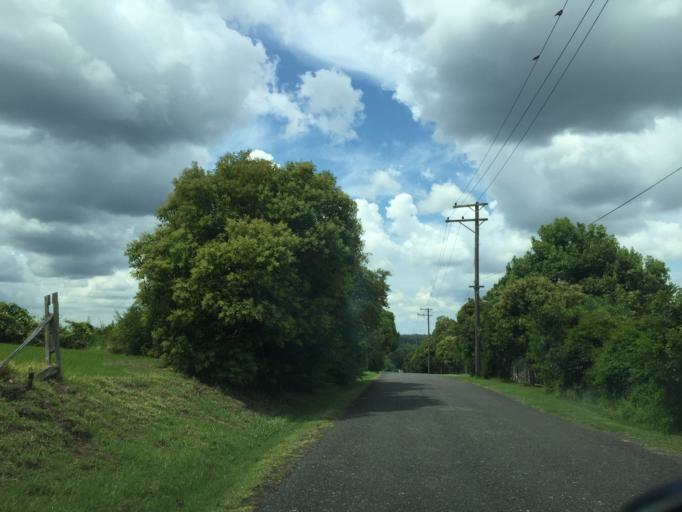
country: AU
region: New South Wales
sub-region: Hornsby Shire
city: Galston
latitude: -33.6546
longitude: 151.0523
